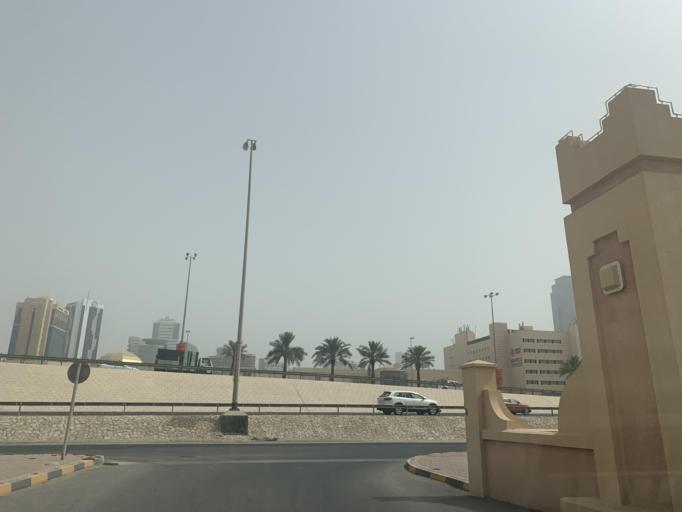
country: BH
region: Manama
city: Jidd Hafs
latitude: 26.2304
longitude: 50.5378
